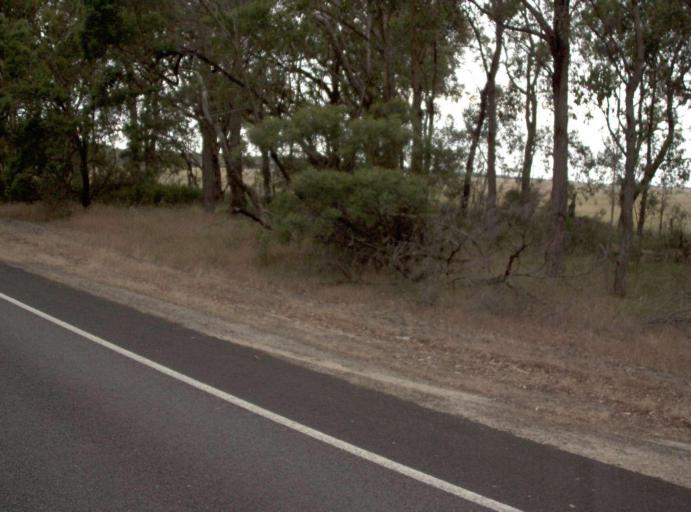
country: AU
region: Victoria
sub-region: Wellington
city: Sale
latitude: -38.5100
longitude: 146.8887
